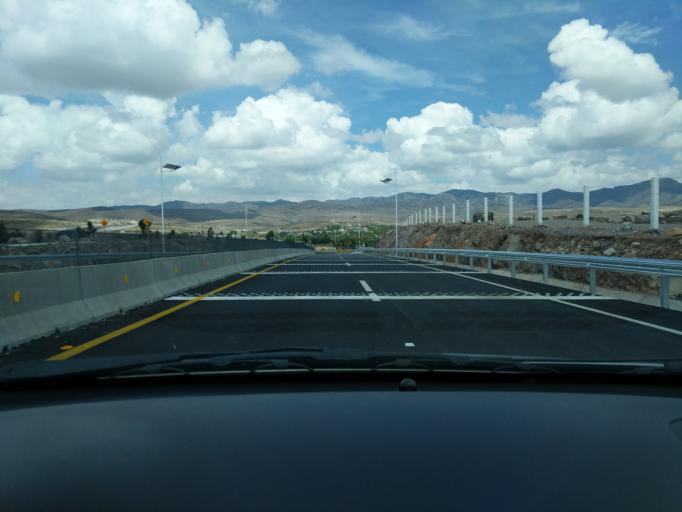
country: MX
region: San Luis Potosi
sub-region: Mexquitic de Carmona
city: Guadalupe Victoria
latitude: 22.1641
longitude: -101.0577
